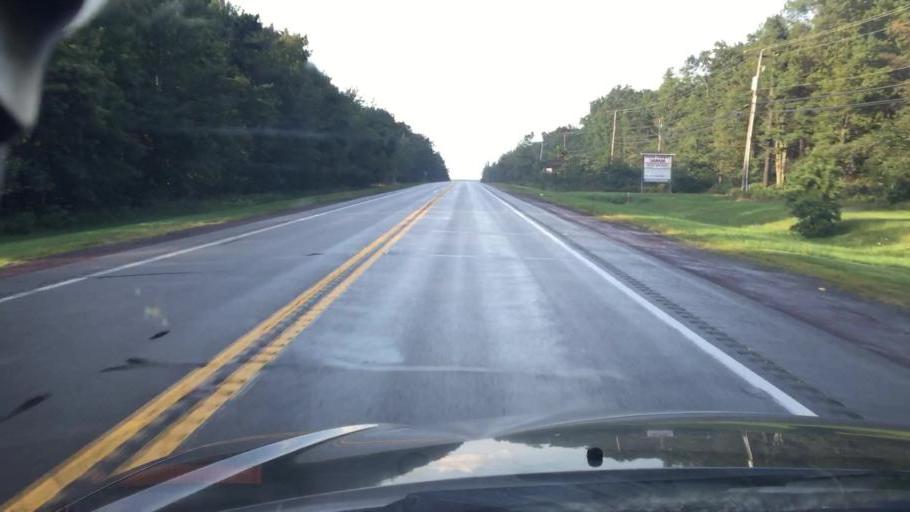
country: US
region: Pennsylvania
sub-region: Carbon County
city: Towamensing Trails
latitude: 40.9401
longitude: -75.6555
